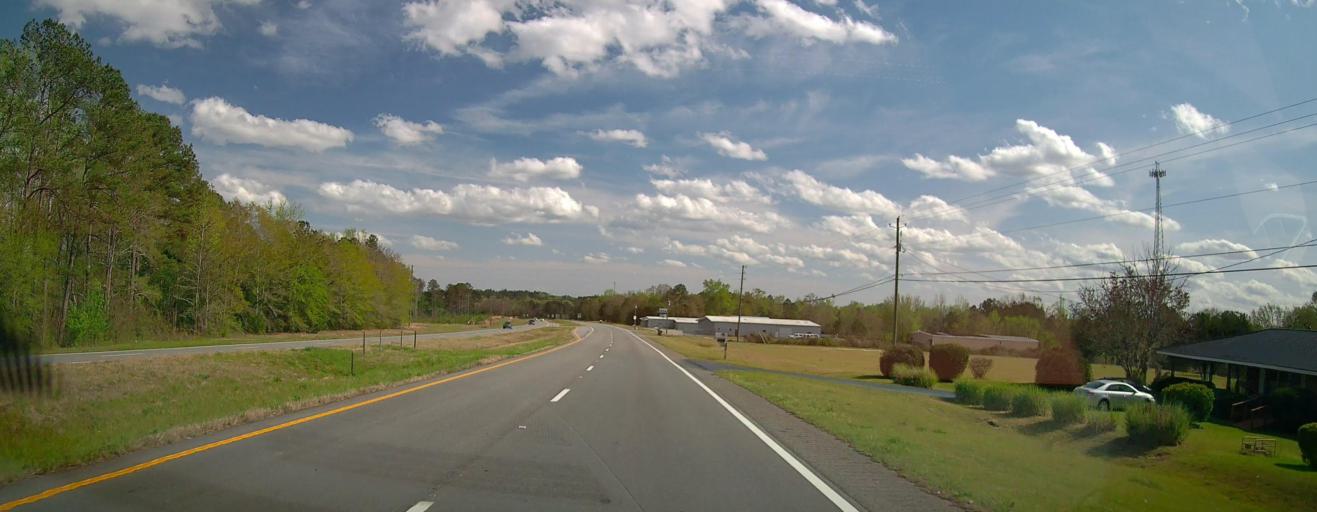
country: US
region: Georgia
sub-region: Baldwin County
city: Hardwick
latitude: 33.0145
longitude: -83.2264
